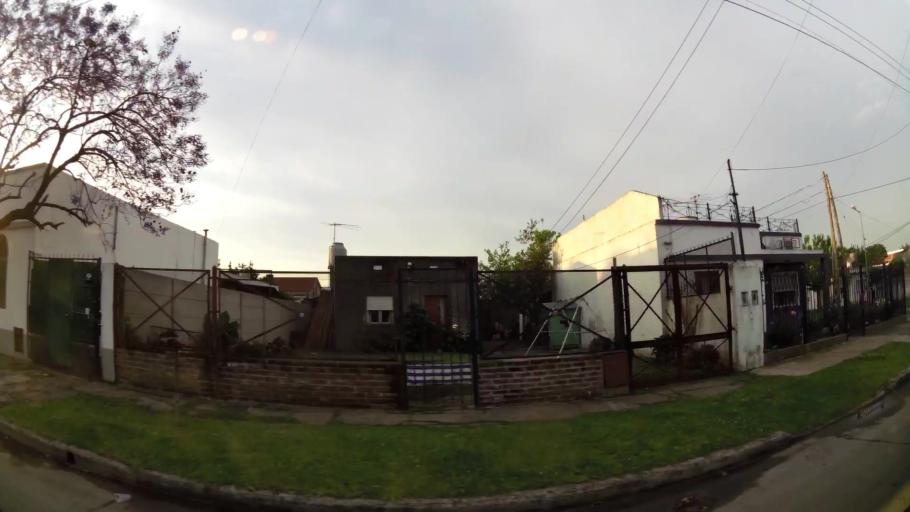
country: AR
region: Buenos Aires
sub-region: Partido de Almirante Brown
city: Adrogue
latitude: -34.7631
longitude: -58.3535
